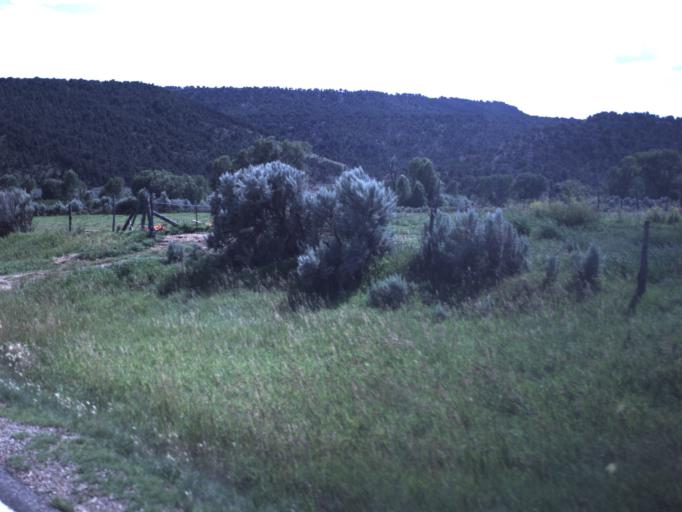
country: US
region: Utah
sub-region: Duchesne County
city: Duchesne
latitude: 40.3281
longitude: -110.6713
